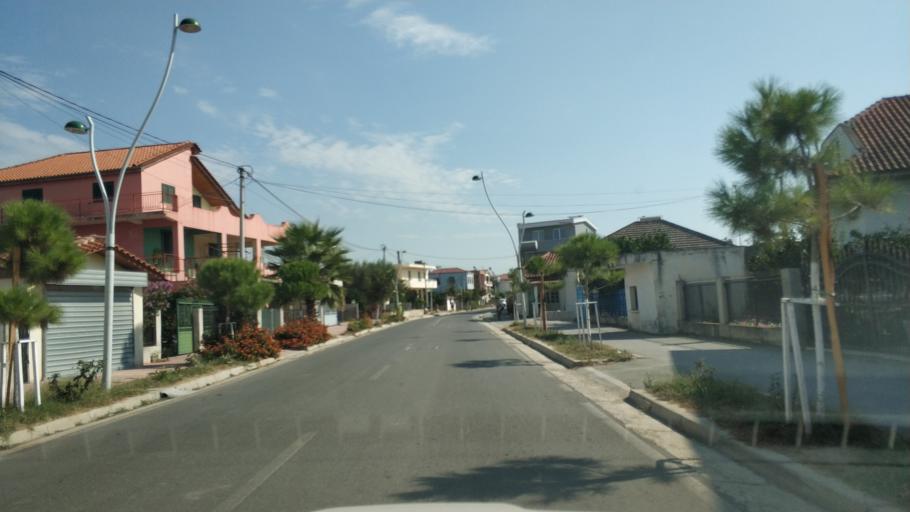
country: AL
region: Fier
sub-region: Rrethi i Lushnjes
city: Divjake
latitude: 40.9949
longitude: 19.5268
